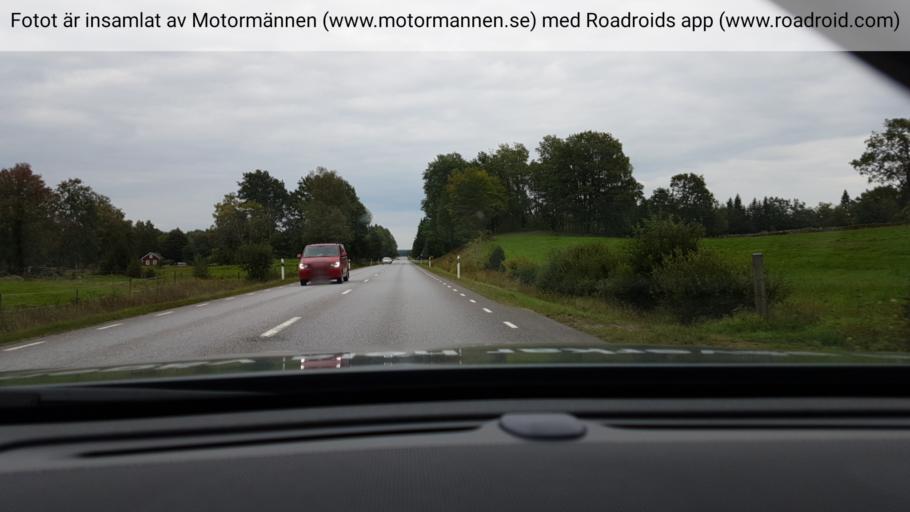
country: SE
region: Joenkoeping
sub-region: Gislaveds Kommun
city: Reftele
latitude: 57.1576
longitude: 13.5061
